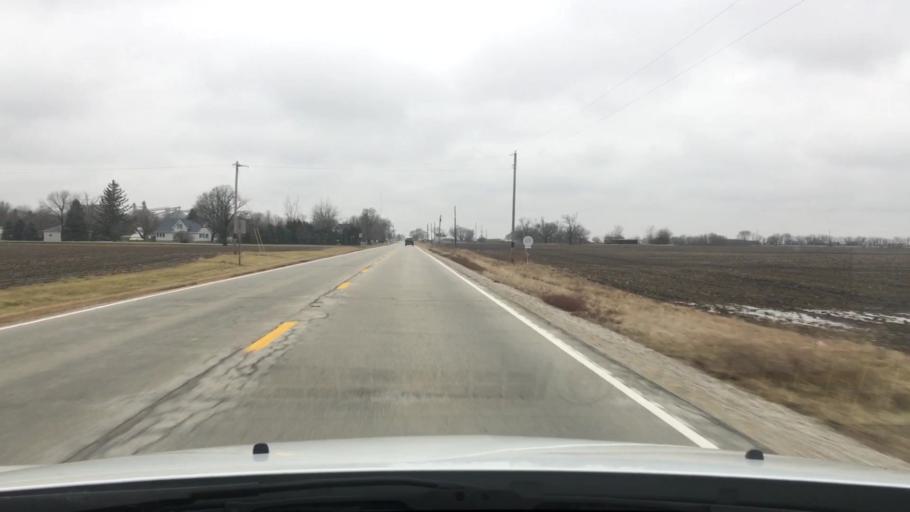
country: US
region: Illinois
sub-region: Iroquois County
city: Clifton
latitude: 40.8850
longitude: -87.9435
